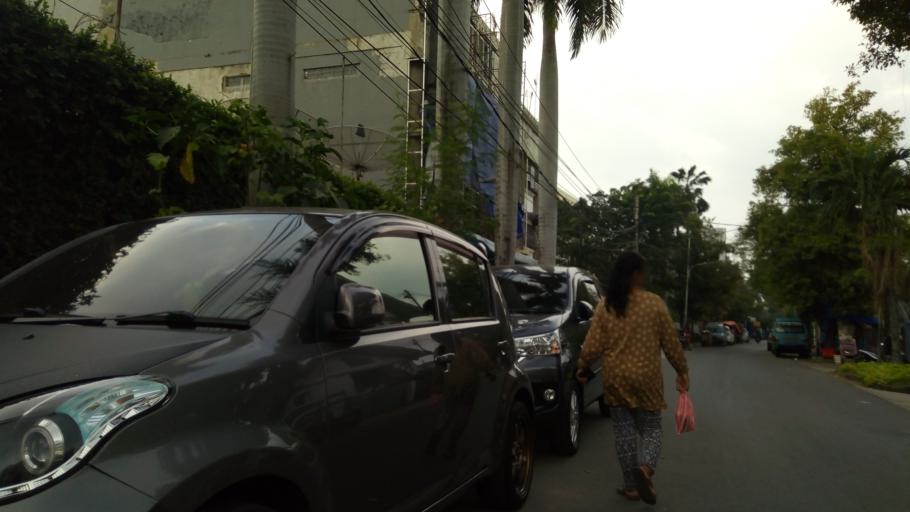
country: ID
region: Jakarta Raya
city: Jakarta
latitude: -6.1528
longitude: 106.8337
